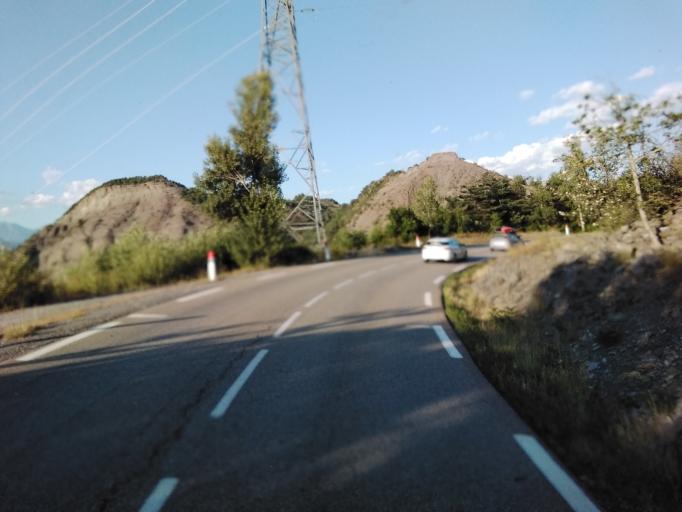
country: FR
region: Provence-Alpes-Cote d'Azur
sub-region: Departement des Hautes-Alpes
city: Chorges
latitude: 44.4637
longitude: 6.2682
